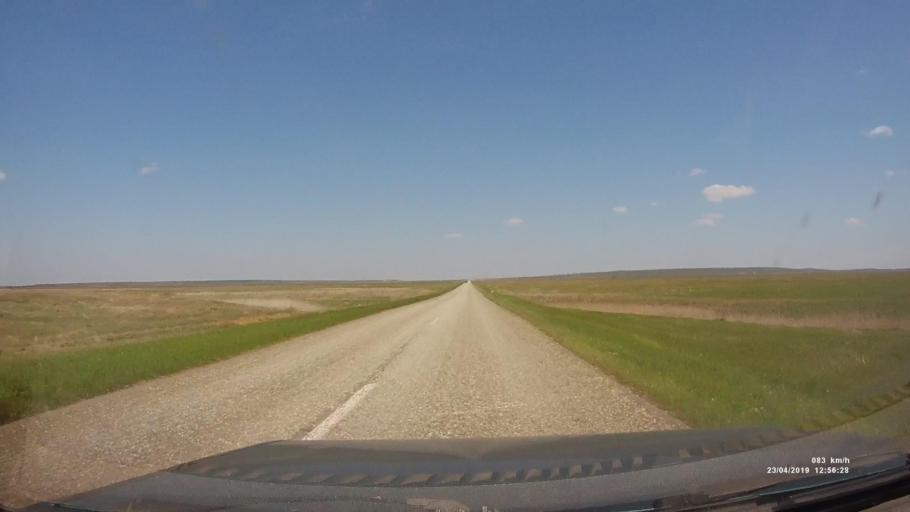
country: RU
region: Kalmykiya
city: Yashalta
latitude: 46.5941
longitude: 42.5716
